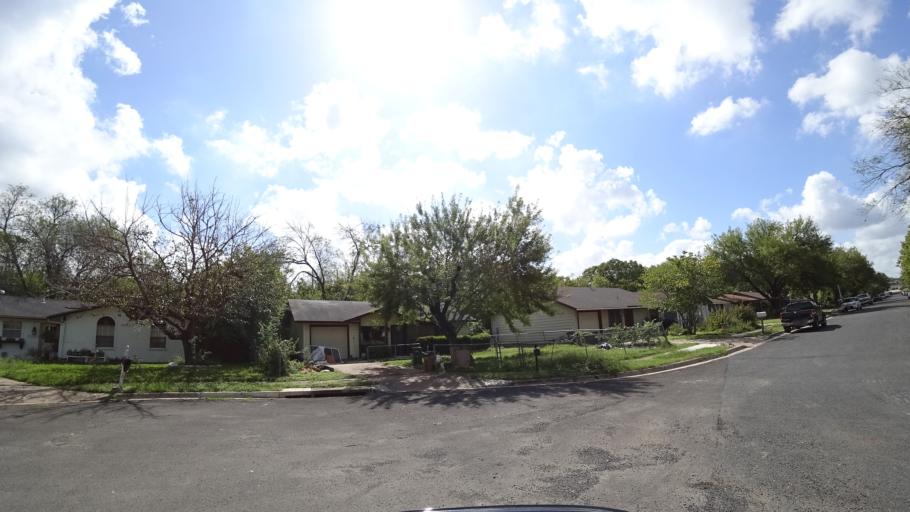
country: US
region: Texas
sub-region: Travis County
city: Onion Creek
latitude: 30.2012
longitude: -97.8029
